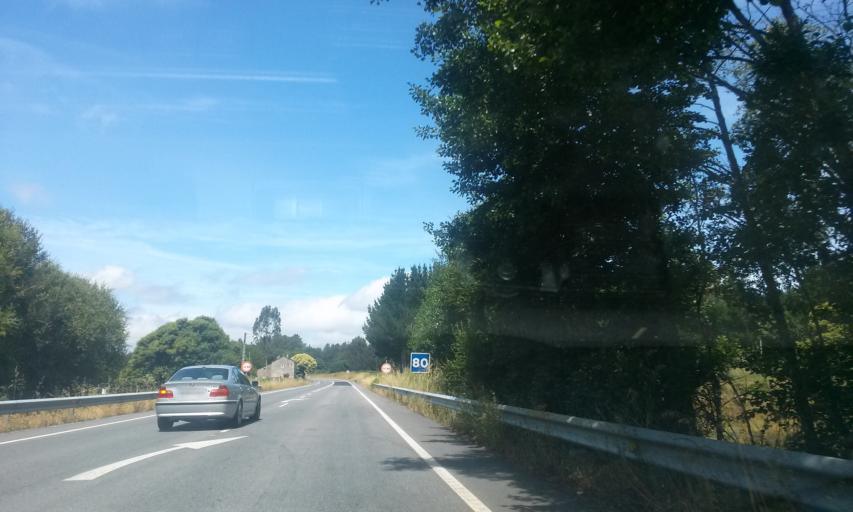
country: ES
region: Galicia
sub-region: Provincia de Lugo
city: Lugo
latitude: 43.0125
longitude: -7.6533
